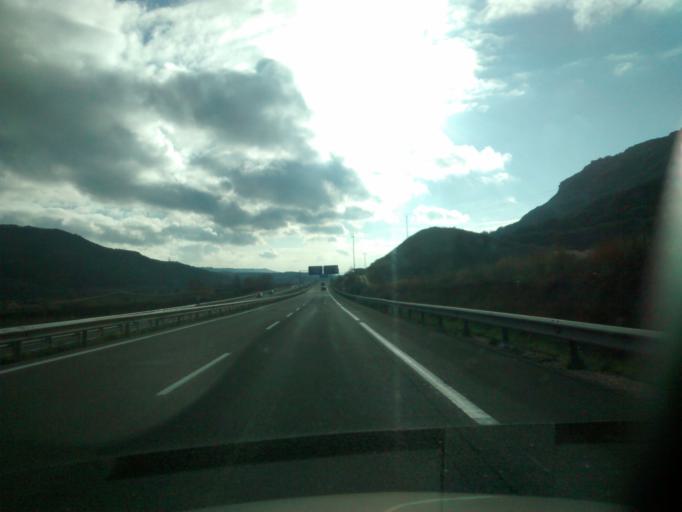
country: ES
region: Castille-La Mancha
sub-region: Provincia de Guadalajara
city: Tortola de Henares
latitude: 40.6764
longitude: -3.0989
